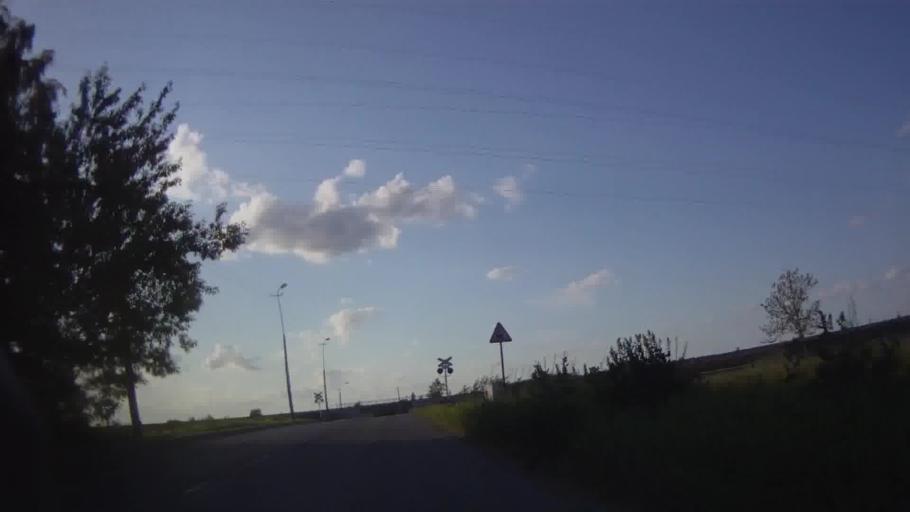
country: LV
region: Rezekne
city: Rezekne
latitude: 56.5208
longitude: 27.3197
